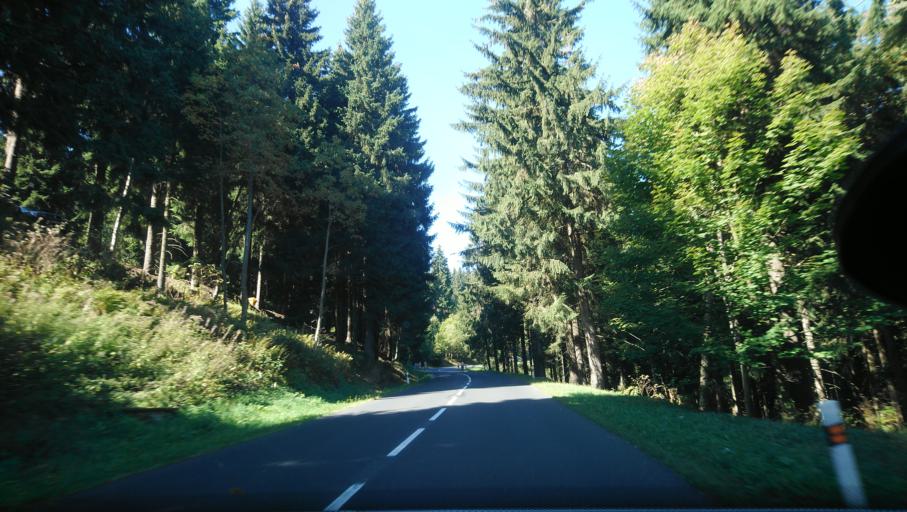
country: DE
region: Saxony
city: Kurort Oberwiesenthal
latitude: 50.4025
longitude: 12.9728
